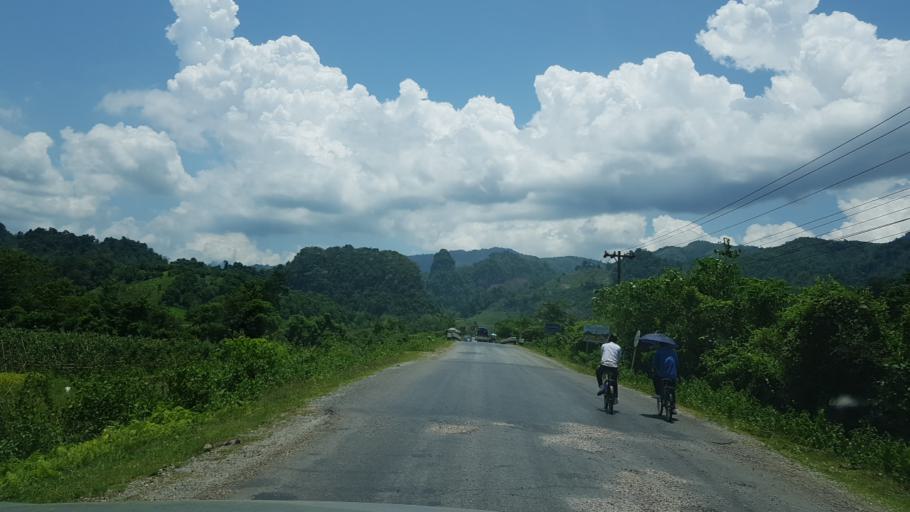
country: LA
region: Vientiane
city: Muang Kasi
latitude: 19.1267
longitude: 102.2447
